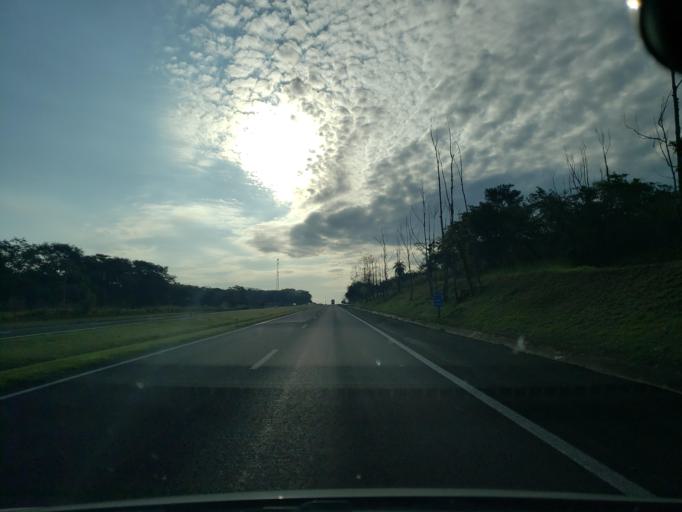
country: BR
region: Sao Paulo
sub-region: Valparaiso
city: Valparaiso
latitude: -21.1761
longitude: -50.9266
